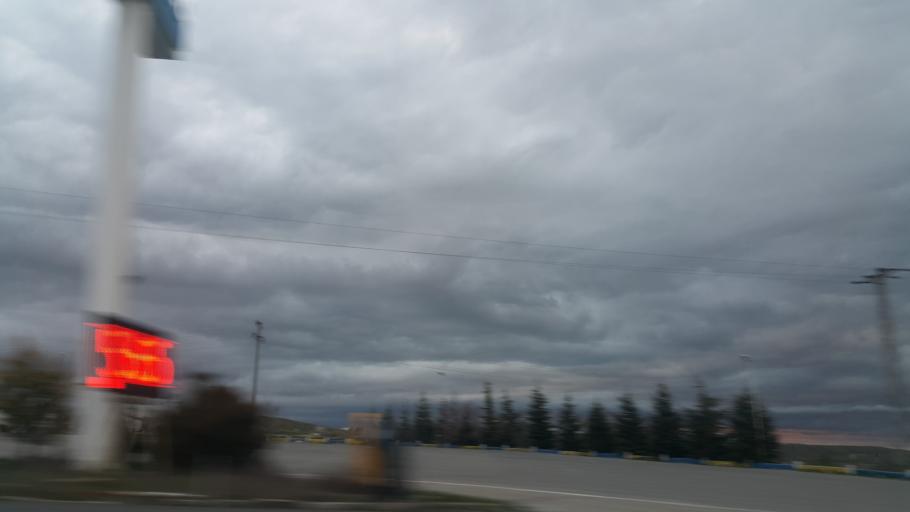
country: TR
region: Ankara
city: Ikizce
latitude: 39.5298
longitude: 32.8615
